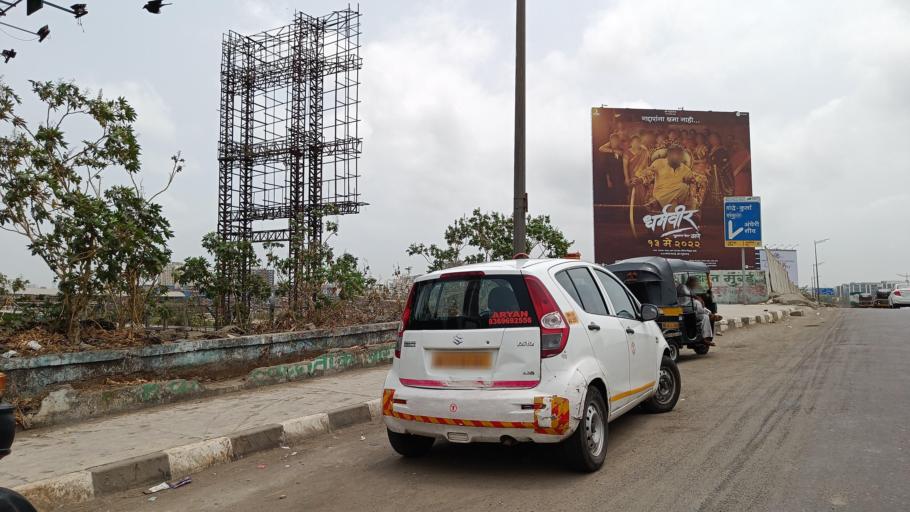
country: IN
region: Maharashtra
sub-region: Mumbai Suburban
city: Mumbai
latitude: 19.0514
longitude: 72.8412
